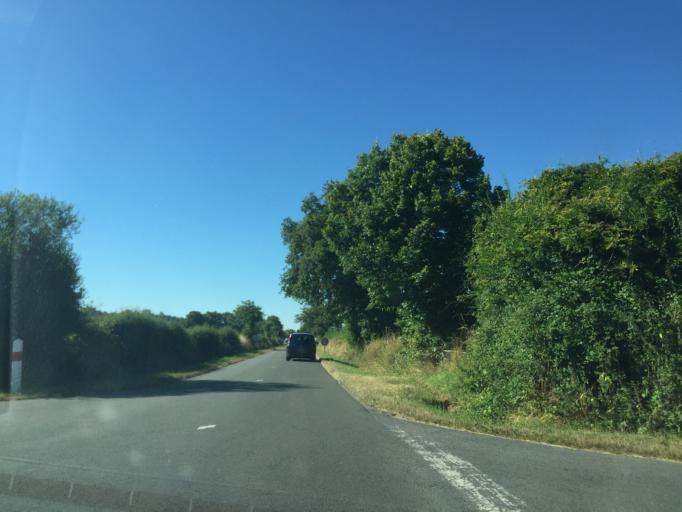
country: FR
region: Auvergne
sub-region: Departement de l'Allier
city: Dompierre-sur-Besbre
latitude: 46.5166
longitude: 3.6216
